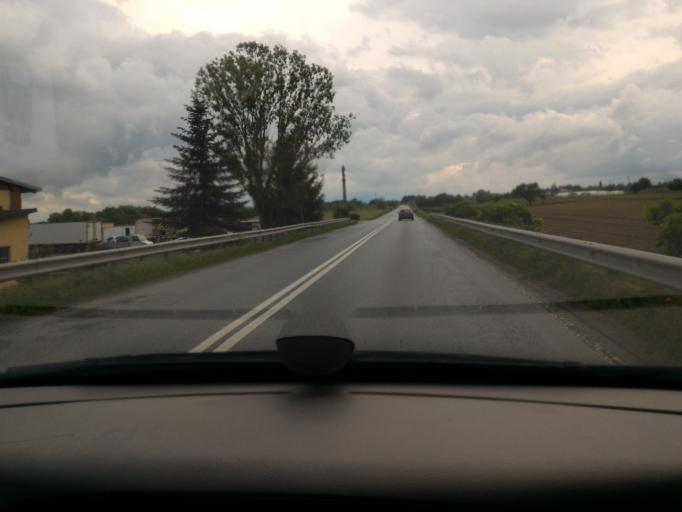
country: IT
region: Piedmont
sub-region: Provincia di Cuneo
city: Savigliano
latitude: 44.6336
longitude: 7.6650
